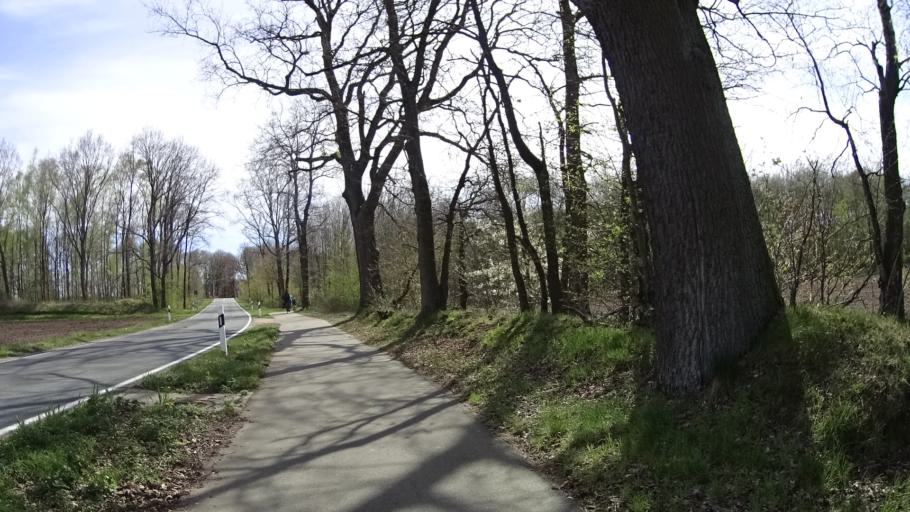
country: DE
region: Lower Saxony
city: Spelle
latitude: 52.3299
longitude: 7.4528
